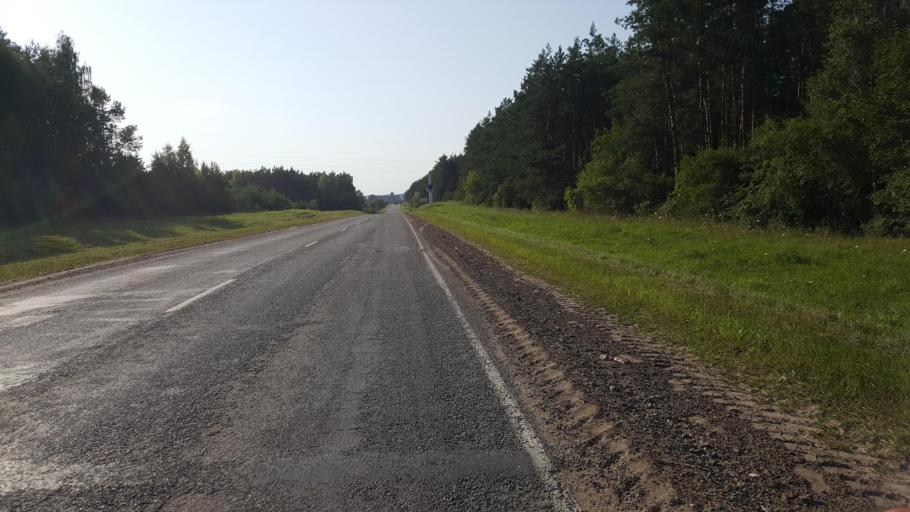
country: BY
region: Brest
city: Kamyanyets
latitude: 52.3895
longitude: 23.8420
